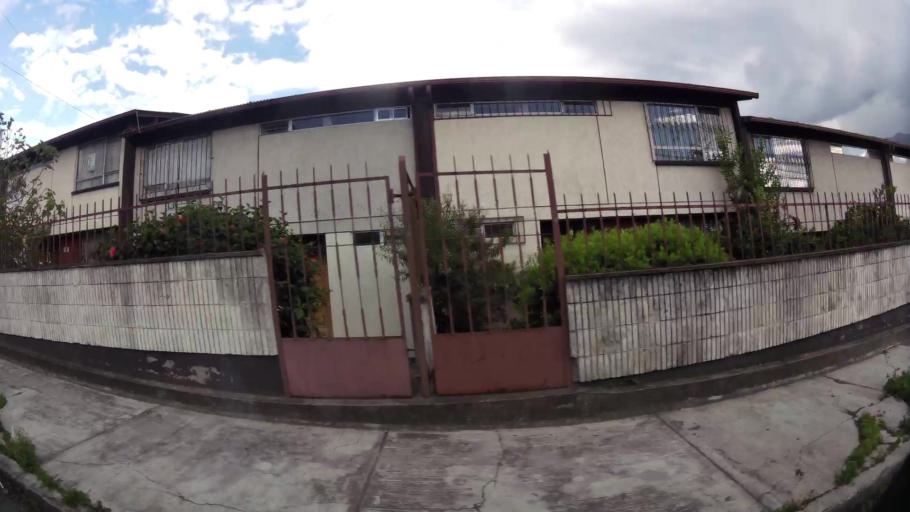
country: EC
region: Pichincha
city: Quito
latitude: -0.1333
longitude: -78.4830
